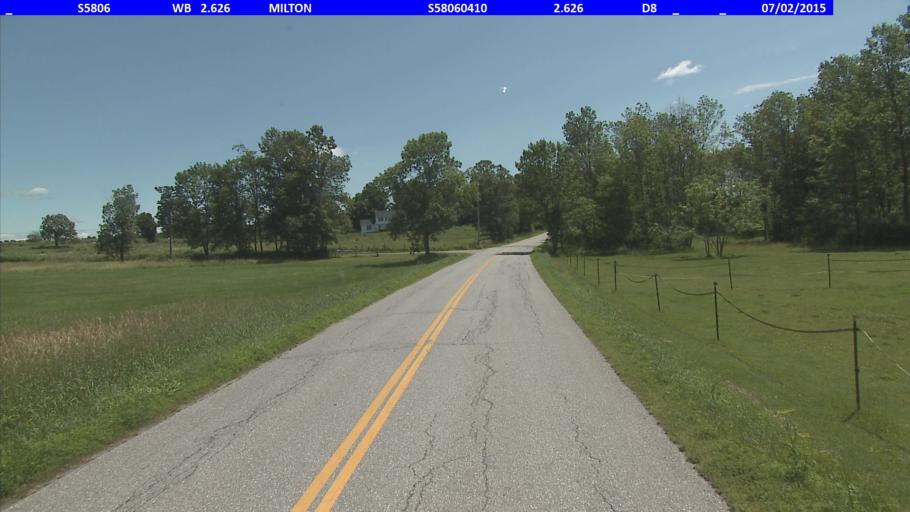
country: US
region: Vermont
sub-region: Chittenden County
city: Milton
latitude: 44.6668
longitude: -73.1601
